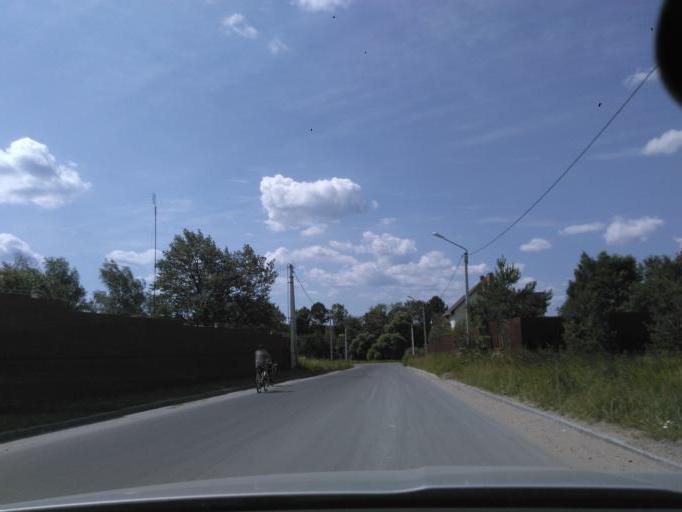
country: RU
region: Moskovskaya
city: Solnechnogorsk
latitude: 56.1657
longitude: 36.9772
